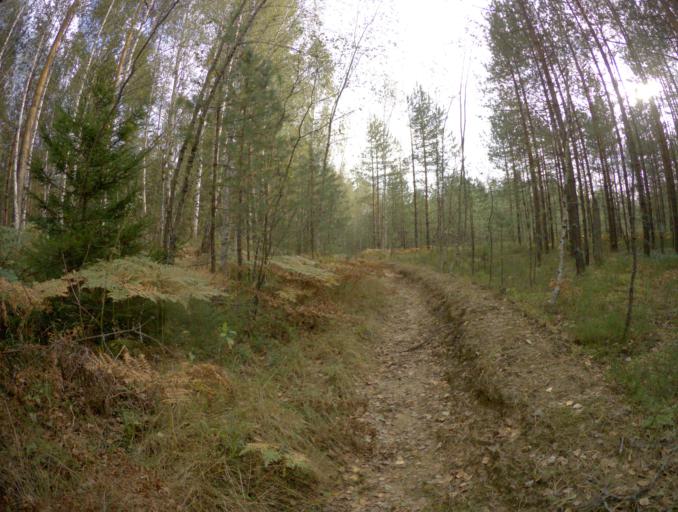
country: RU
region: Vladimir
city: Raduzhnyy
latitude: 55.9718
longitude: 40.2651
